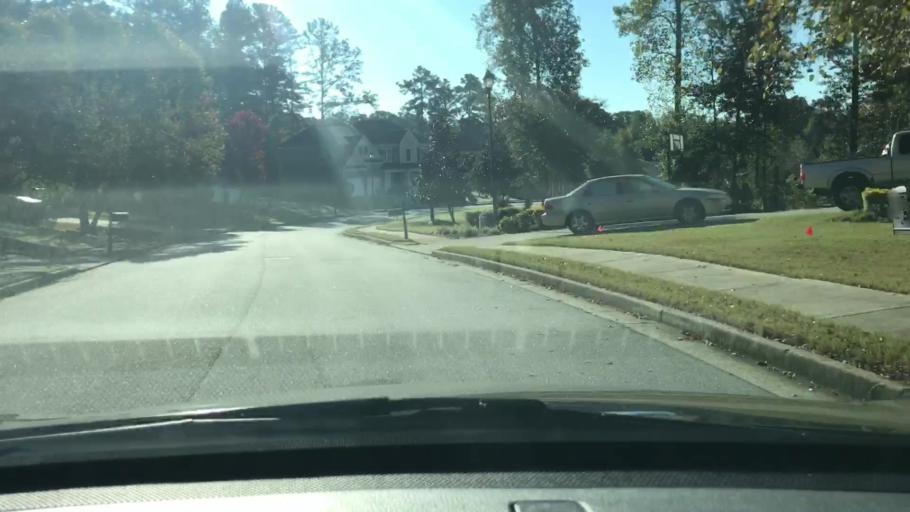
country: US
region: Georgia
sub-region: Douglas County
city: Douglasville
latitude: 33.7394
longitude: -84.7579
